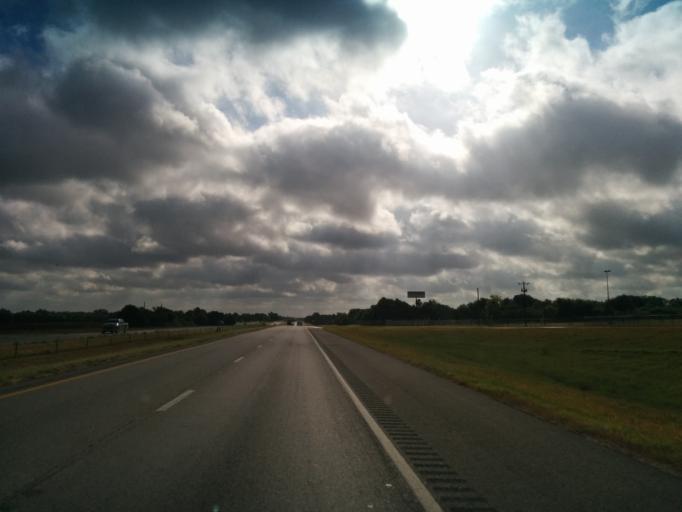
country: US
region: Texas
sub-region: Guadalupe County
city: Cibolo
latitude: 29.4981
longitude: -98.1939
